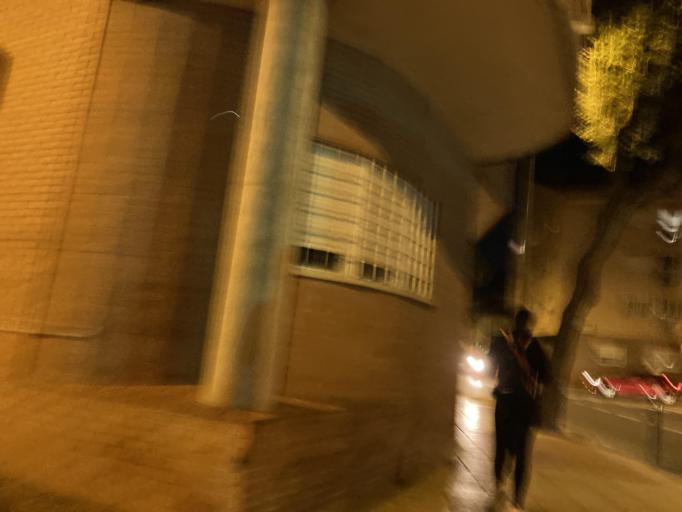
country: ES
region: Murcia
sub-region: Murcia
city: Murcia
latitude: 38.0005
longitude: -1.1254
